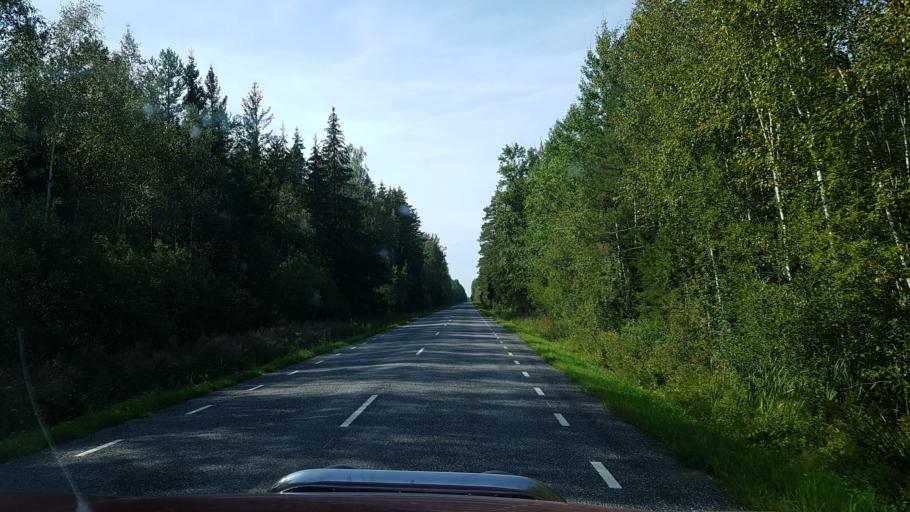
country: EE
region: Viljandimaa
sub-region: Moisakuela linn
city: Moisakula
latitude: 58.3475
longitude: 25.1367
